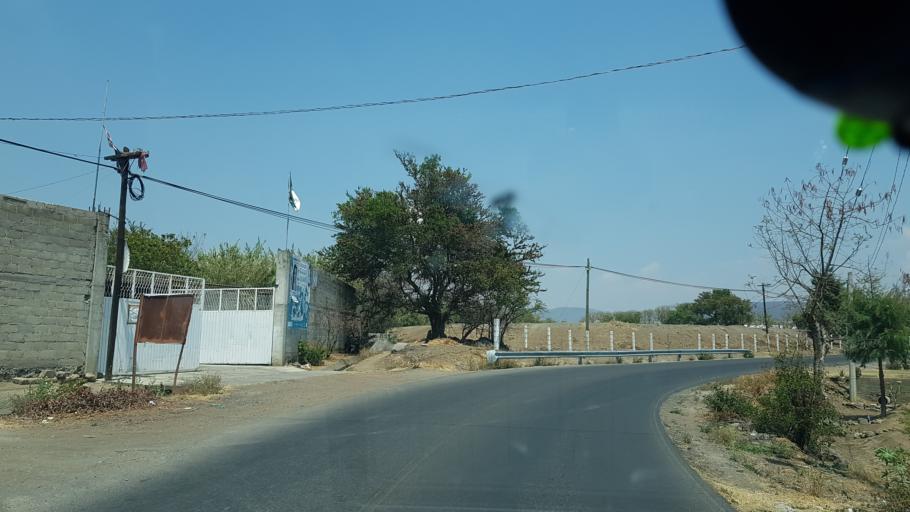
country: MX
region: Puebla
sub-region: Huaquechula
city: Cacaloxuchitl
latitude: 18.7895
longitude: -98.4755
